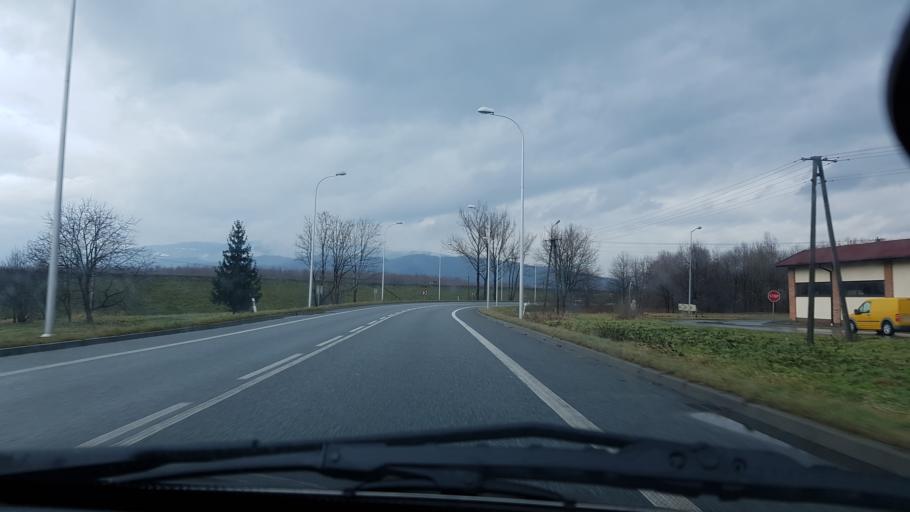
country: PL
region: Silesian Voivodeship
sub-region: Powiat zywiecki
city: Zywiec
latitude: 49.6978
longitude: 19.1989
